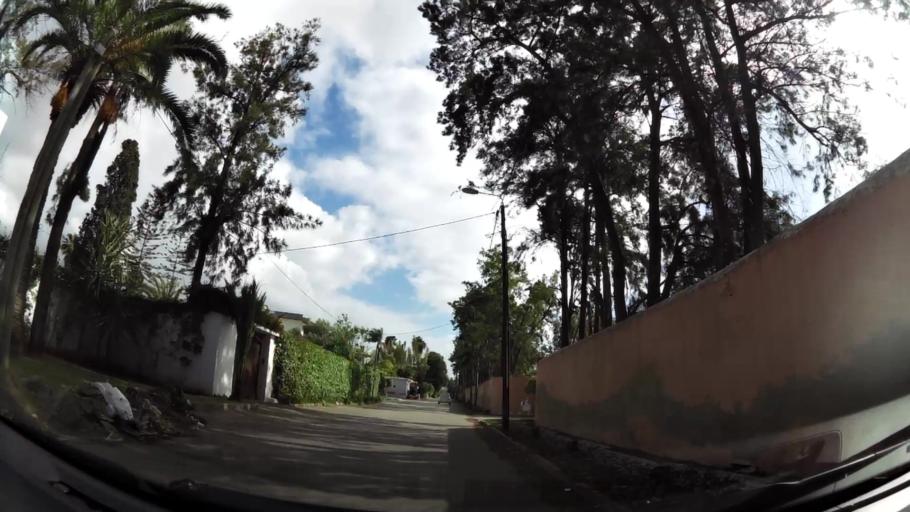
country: MA
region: Grand Casablanca
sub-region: Casablanca
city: Casablanca
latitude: 33.5467
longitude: -7.6251
